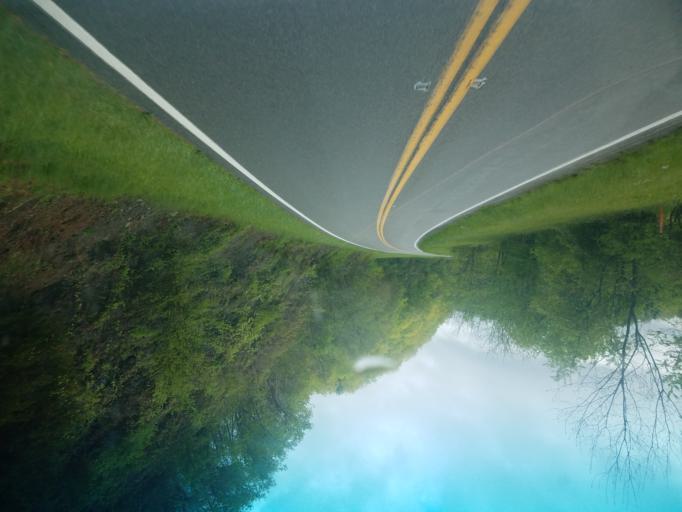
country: US
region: Virginia
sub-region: Washington County
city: Emory
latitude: 36.6610
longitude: -81.8067
